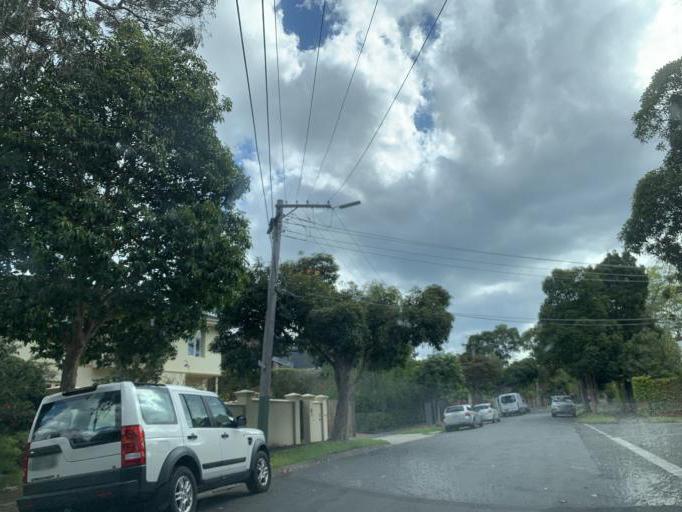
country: AU
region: Victoria
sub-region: Bayside
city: North Brighton
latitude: -37.9169
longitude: 145.0115
